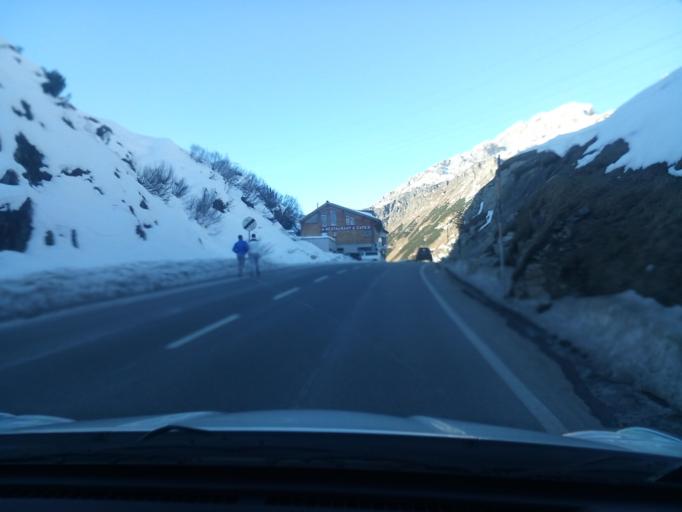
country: AT
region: Tyrol
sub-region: Politischer Bezirk Landeck
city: Sankt Anton am Arlberg
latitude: 47.1281
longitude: 10.2121
